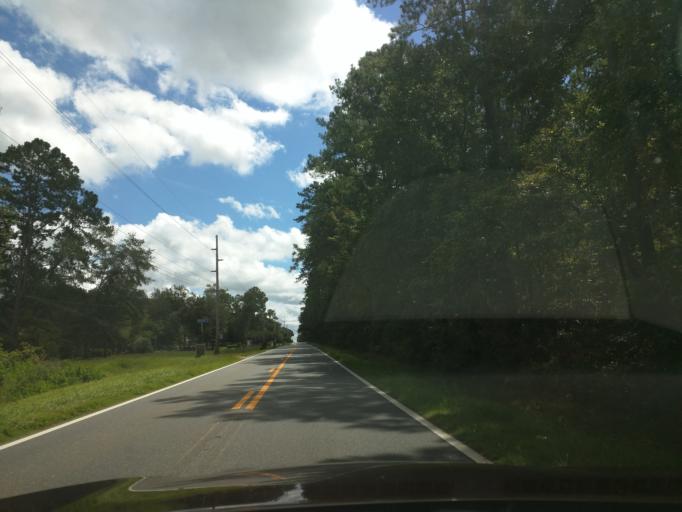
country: US
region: Florida
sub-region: Leon County
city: Tallahassee
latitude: 30.5364
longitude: -84.1420
